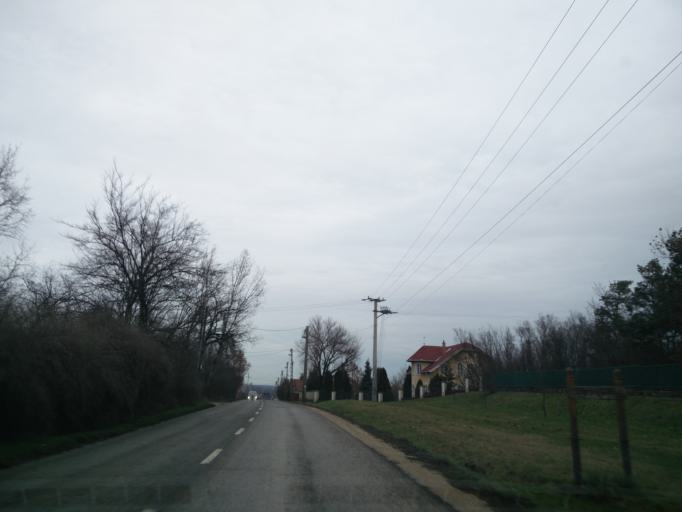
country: HU
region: Pest
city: Gyomro
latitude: 47.4117
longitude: 19.3879
